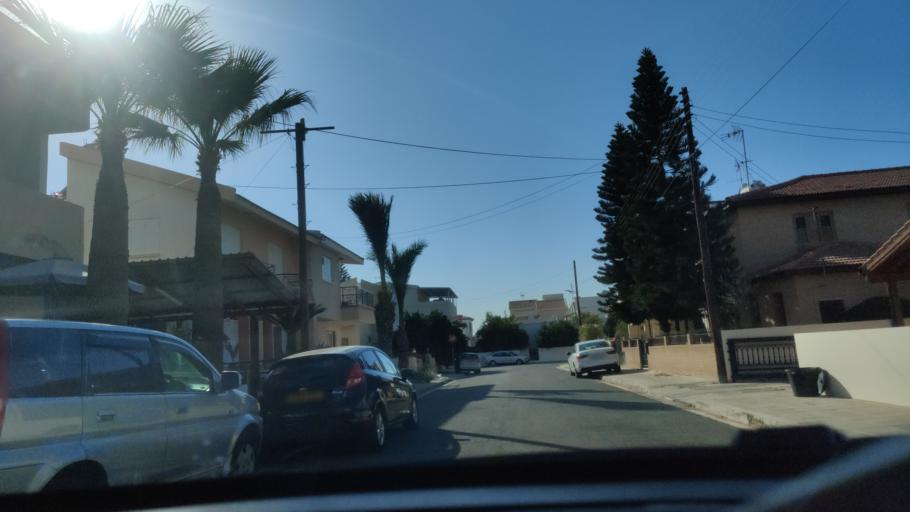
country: CY
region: Lefkosia
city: Tseri
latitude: 35.1200
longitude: 33.3258
